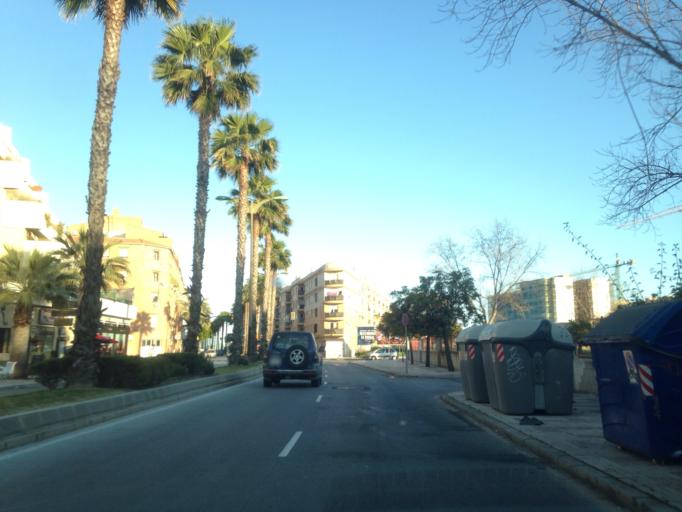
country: ES
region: Andalusia
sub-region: Provincia de Malaga
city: Malaga
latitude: 36.6865
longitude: -4.4524
